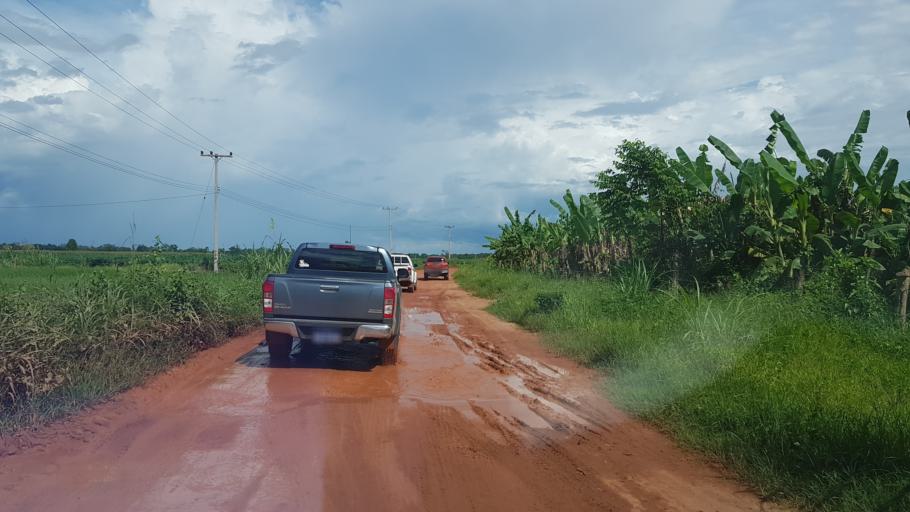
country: LA
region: Vientiane
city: Vientiane
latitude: 18.2235
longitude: 102.5677
